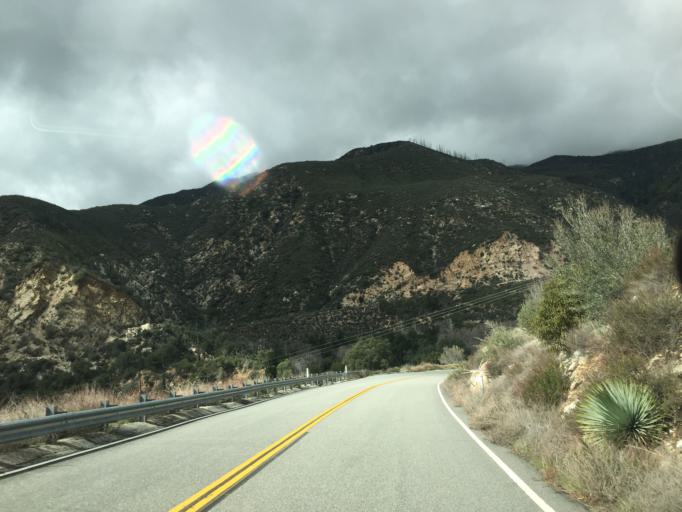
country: US
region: California
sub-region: Los Angeles County
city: Glendora
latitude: 34.2891
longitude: -117.8373
